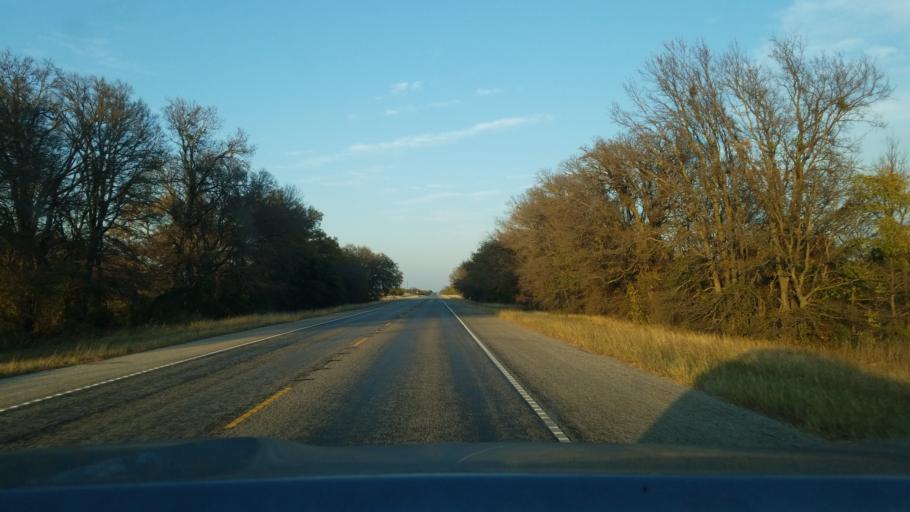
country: US
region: Texas
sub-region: Eastland County
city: Cisco
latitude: 32.4138
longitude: -98.9434
